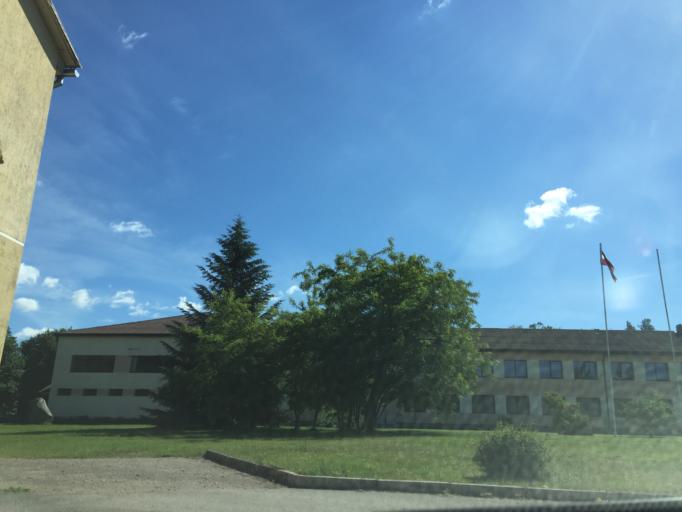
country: LV
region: Dundaga
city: Dundaga
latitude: 57.3546
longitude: 22.0617
